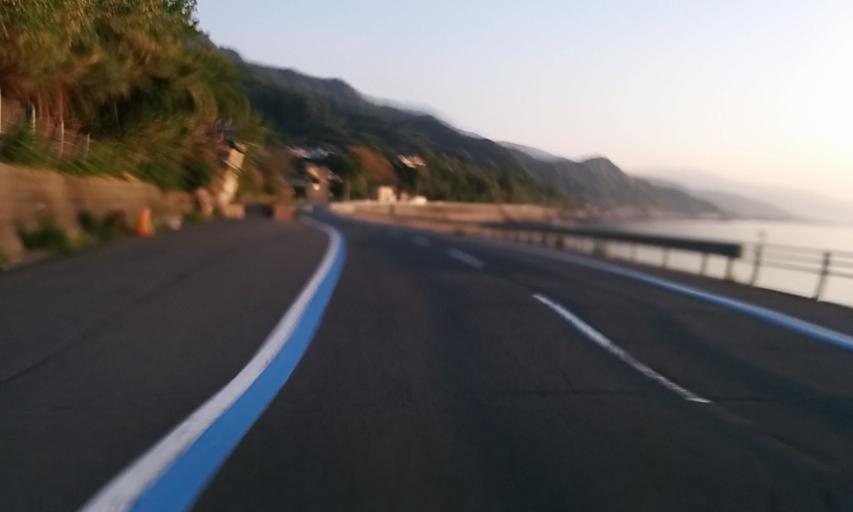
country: JP
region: Ehime
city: Iyo
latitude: 33.7054
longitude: 132.6601
